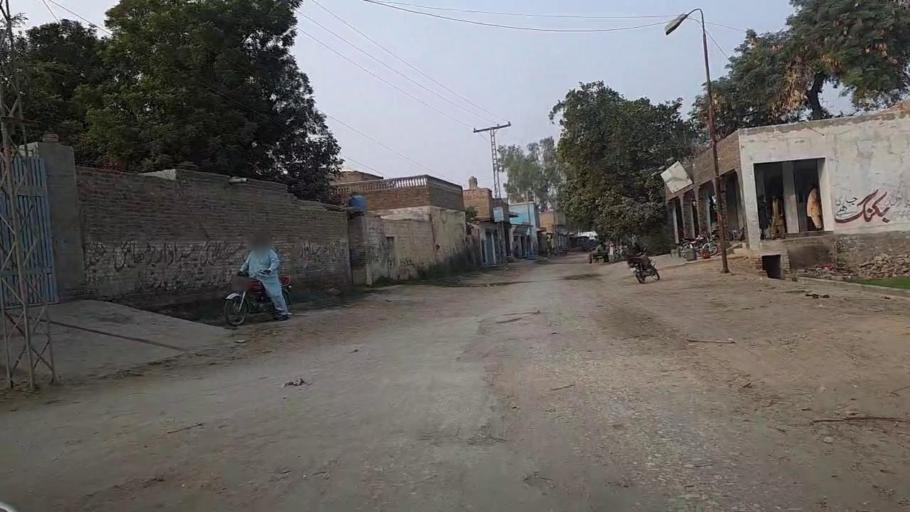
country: PK
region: Sindh
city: Setharja Old
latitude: 27.0851
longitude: 68.4954
